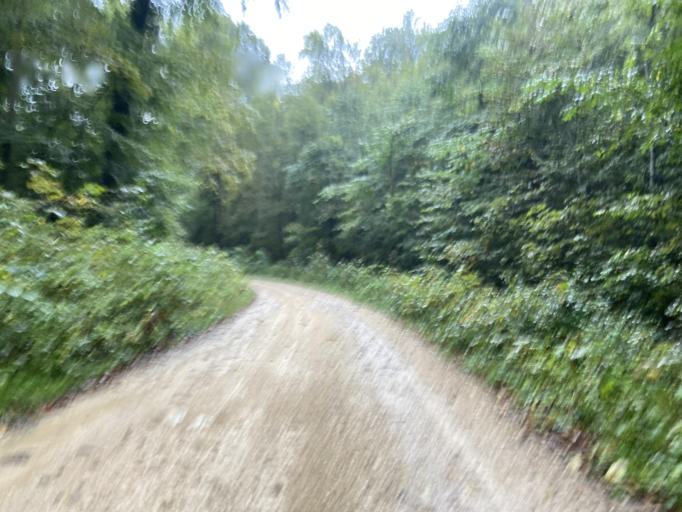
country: DE
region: Baden-Wuerttemberg
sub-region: Tuebingen Region
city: Bingen
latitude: 48.1232
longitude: 9.2544
